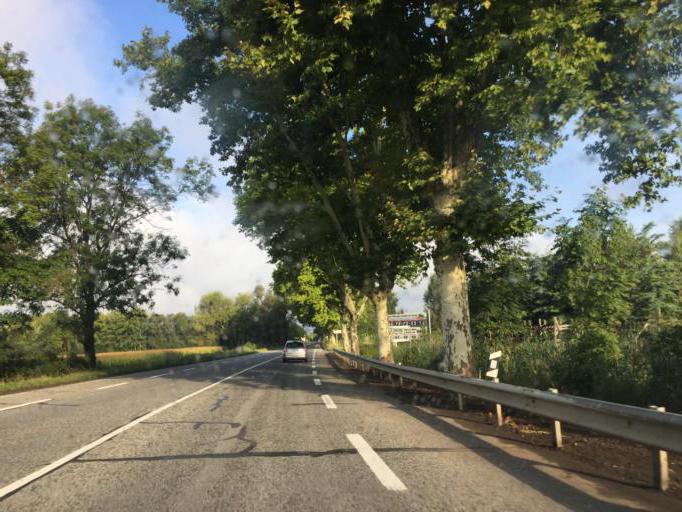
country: FR
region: Rhone-Alpes
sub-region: Departement de la Savoie
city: Les Marches
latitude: 45.5084
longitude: 6.0189
